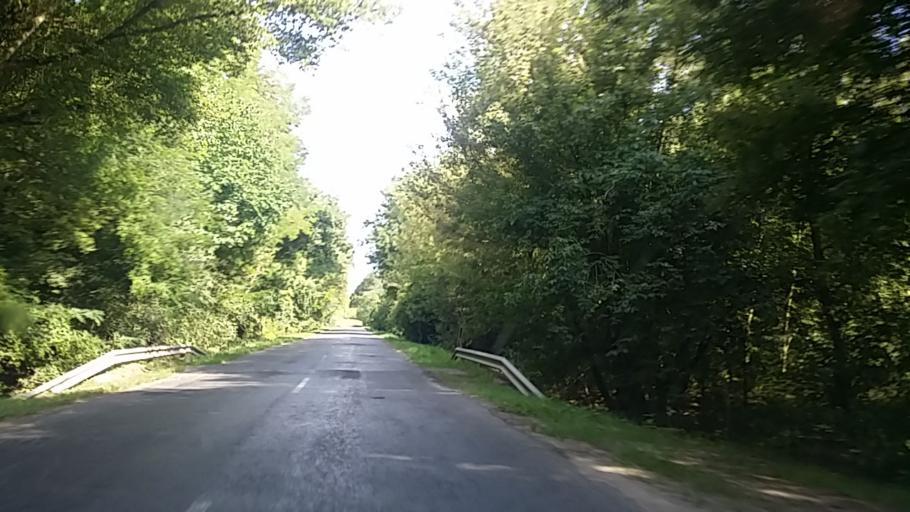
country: HU
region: Tolna
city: Gyonk
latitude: 46.5365
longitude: 18.4987
